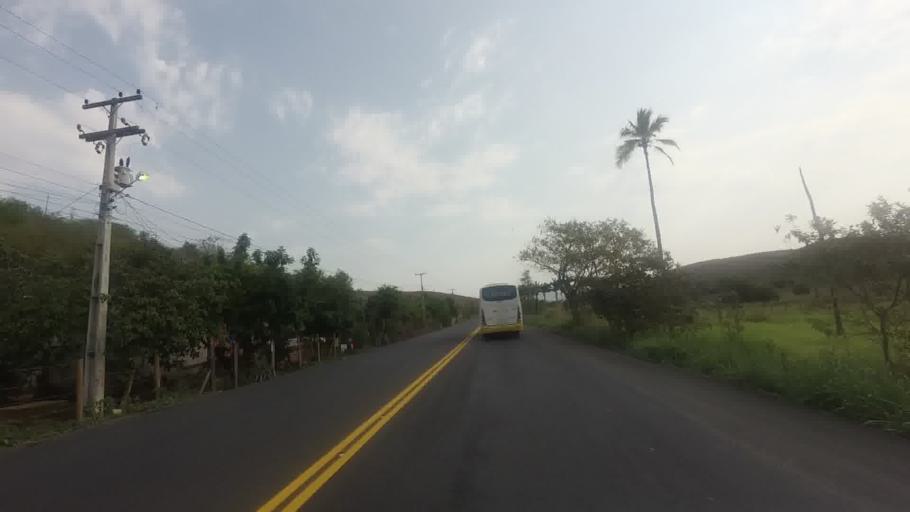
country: BR
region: Rio de Janeiro
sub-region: Itaperuna
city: Itaperuna
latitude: -21.2548
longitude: -41.7659
